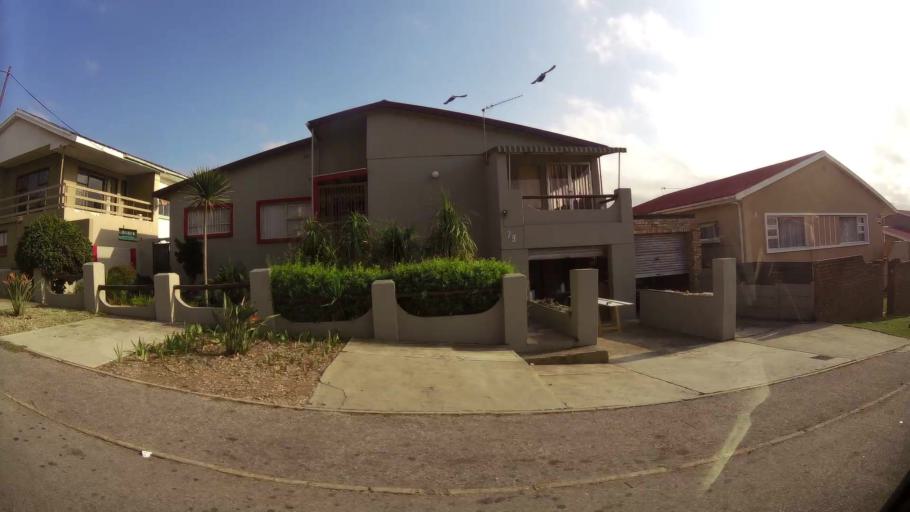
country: ZA
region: Eastern Cape
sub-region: Nelson Mandela Bay Metropolitan Municipality
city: Port Elizabeth
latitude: -33.9239
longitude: 25.5573
